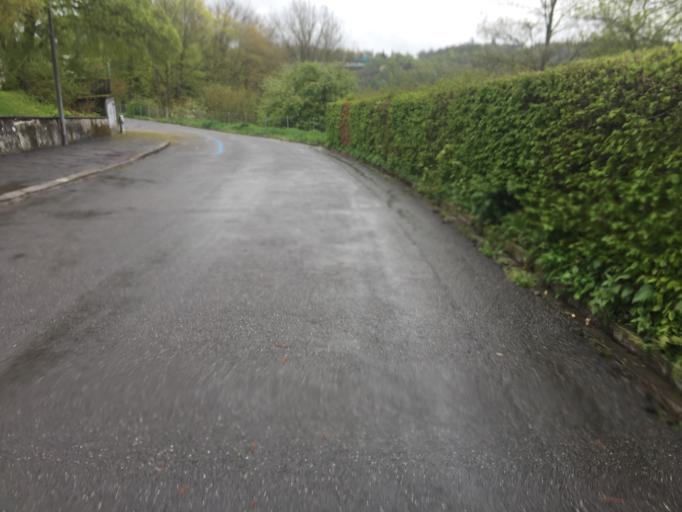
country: CH
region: Bern
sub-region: Bern-Mittelland District
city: Bern
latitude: 46.9731
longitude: 7.4436
